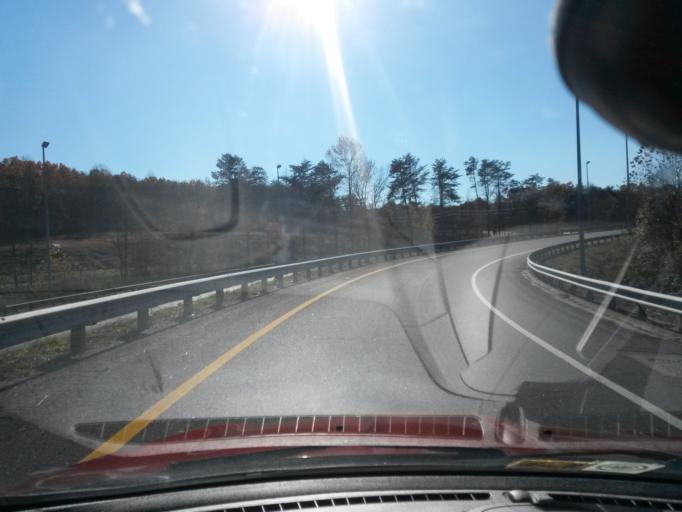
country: US
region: Virginia
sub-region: City of Lynchburg
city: West Lynchburg
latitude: 37.3396
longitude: -79.1862
